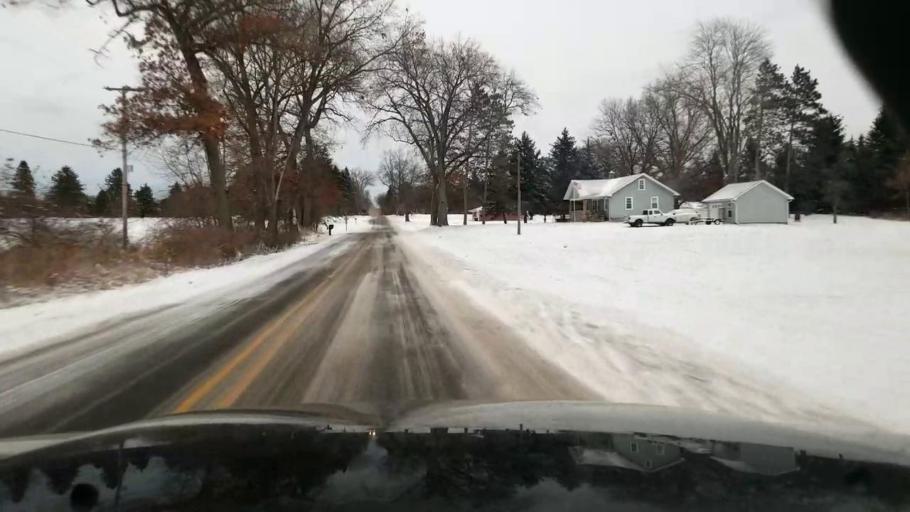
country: US
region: Michigan
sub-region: Jackson County
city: Vandercook Lake
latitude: 42.0947
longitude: -84.4737
